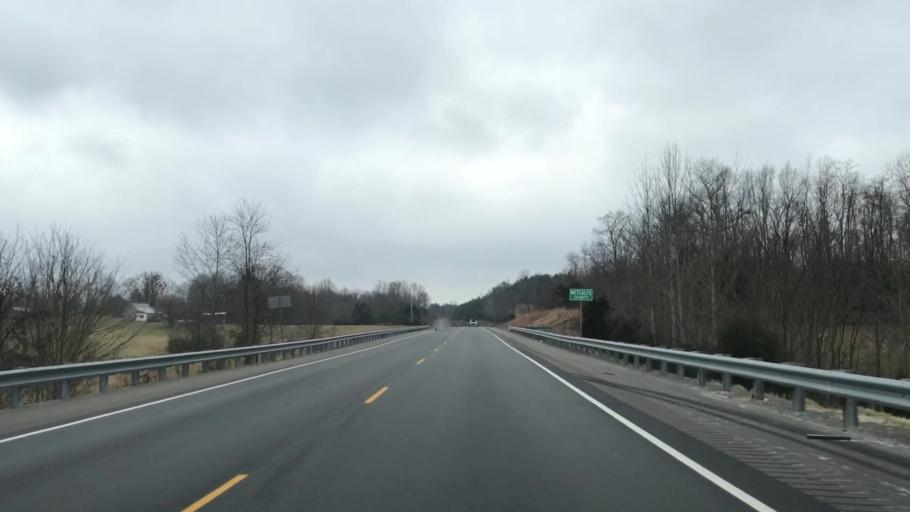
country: US
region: Kentucky
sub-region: Metcalfe County
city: Edmonton
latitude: 36.9545
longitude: -85.4418
